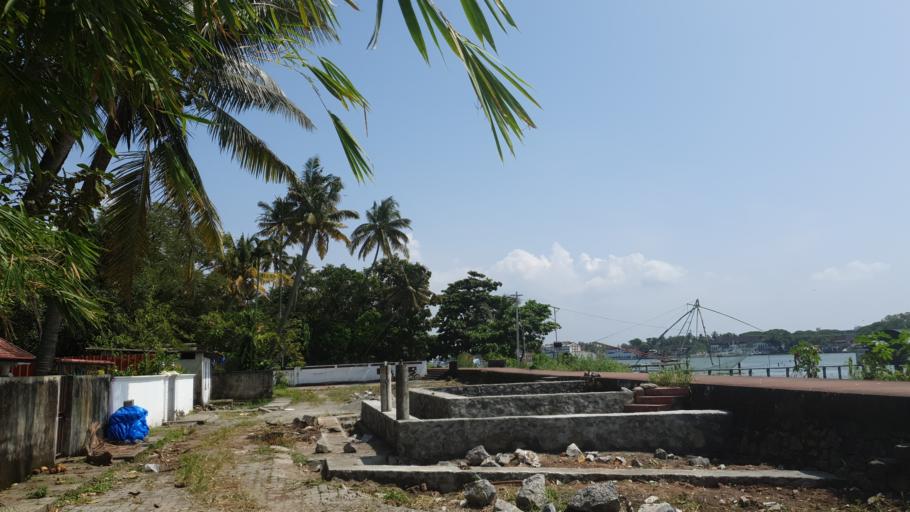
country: IN
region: Kerala
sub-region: Ernakulam
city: Cochin
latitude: 9.9727
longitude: 76.2411
